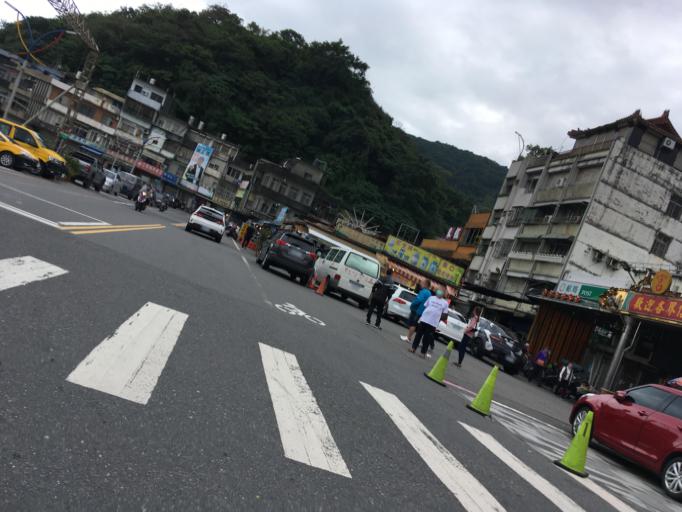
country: TW
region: Taiwan
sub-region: Yilan
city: Yilan
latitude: 24.5821
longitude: 121.8651
